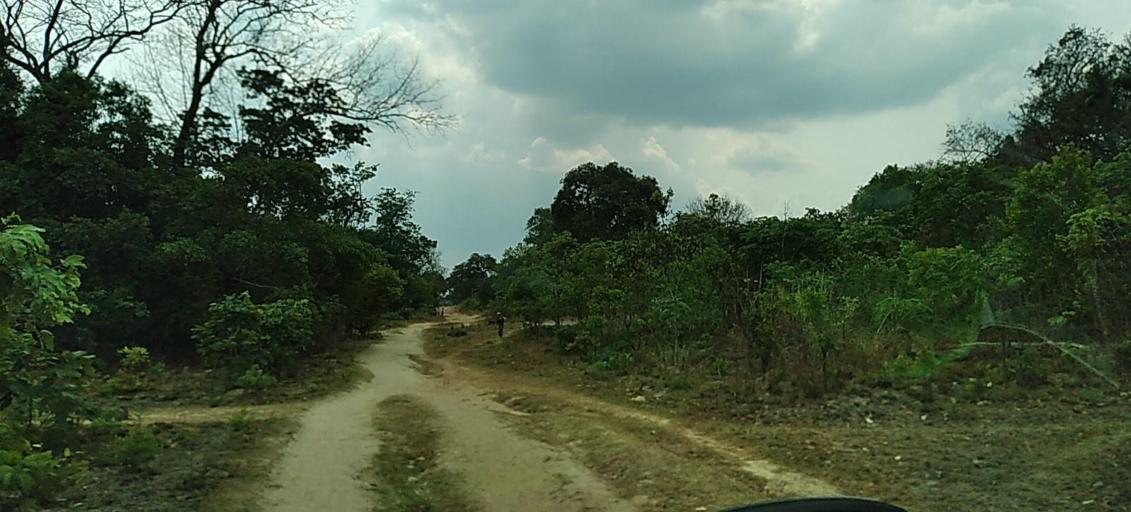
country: ZM
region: North-Western
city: Solwezi
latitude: -12.7869
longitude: 26.5202
